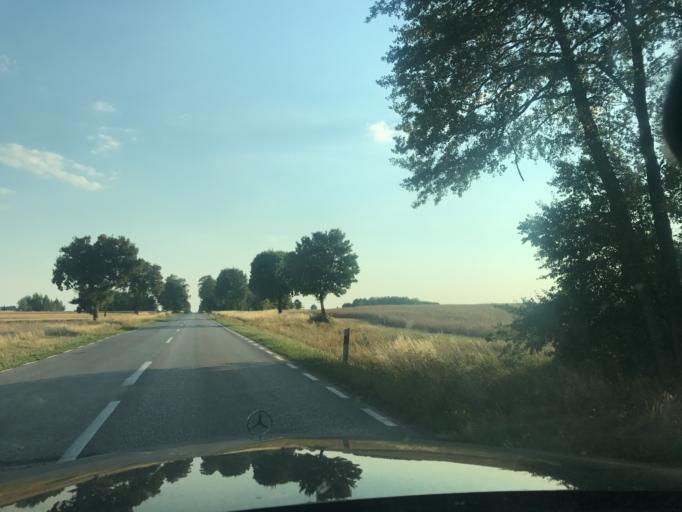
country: PL
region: Lublin Voivodeship
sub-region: Powiat bialski
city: Wisznice
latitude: 51.7765
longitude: 23.2066
